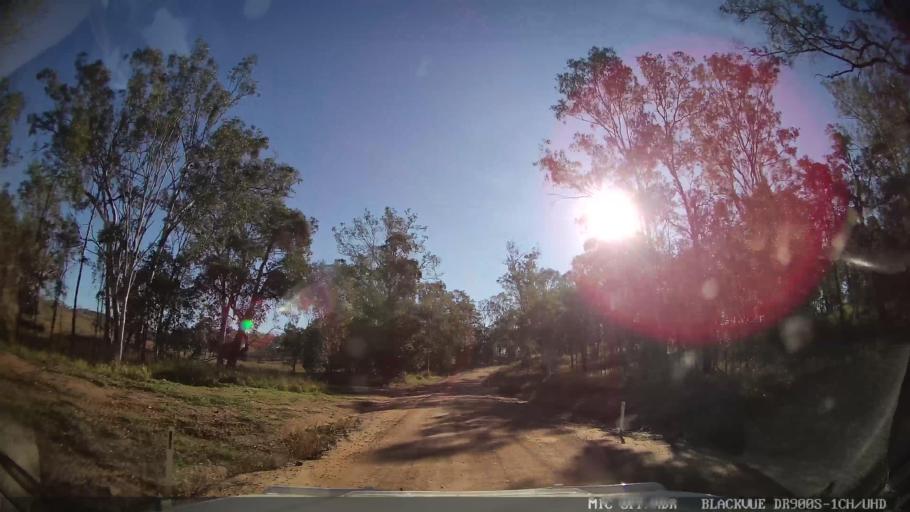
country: AU
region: Queensland
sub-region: Bundaberg
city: Sharon
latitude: -24.7917
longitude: 151.6110
